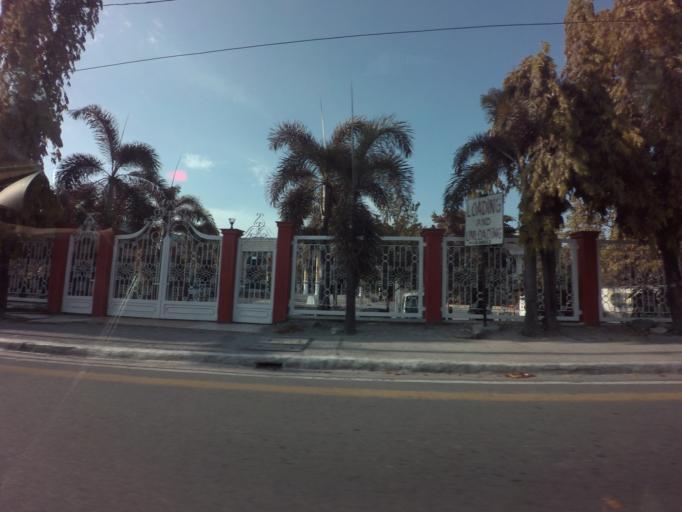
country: PH
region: Calabarzon
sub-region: Province of Rizal
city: Taguig
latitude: 14.4891
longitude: 121.0544
